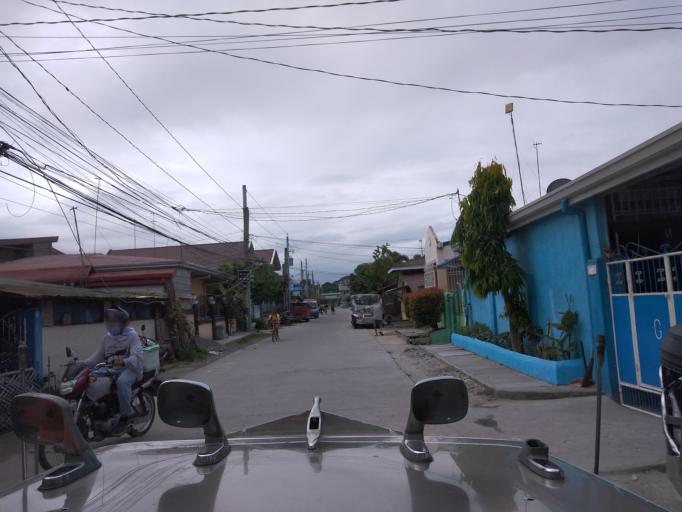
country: PH
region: Central Luzon
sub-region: Province of Pampanga
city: Mexico
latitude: 15.0641
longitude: 120.7178
